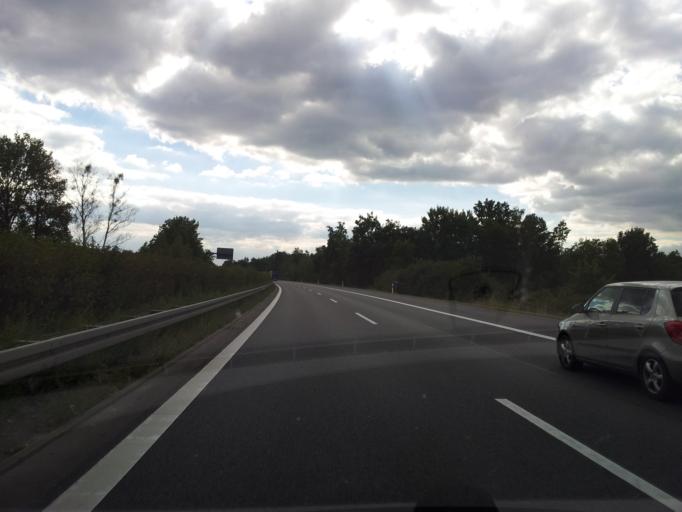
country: DE
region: Brandenburg
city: Grossraschen
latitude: 51.5821
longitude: 13.9339
